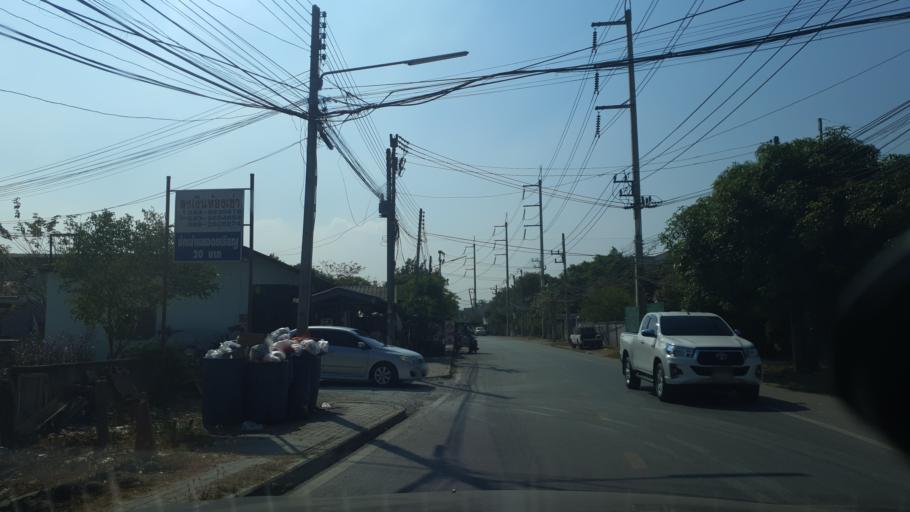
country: TH
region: Nakhon Pathom
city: Salaya
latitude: 13.7818
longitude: 100.2694
